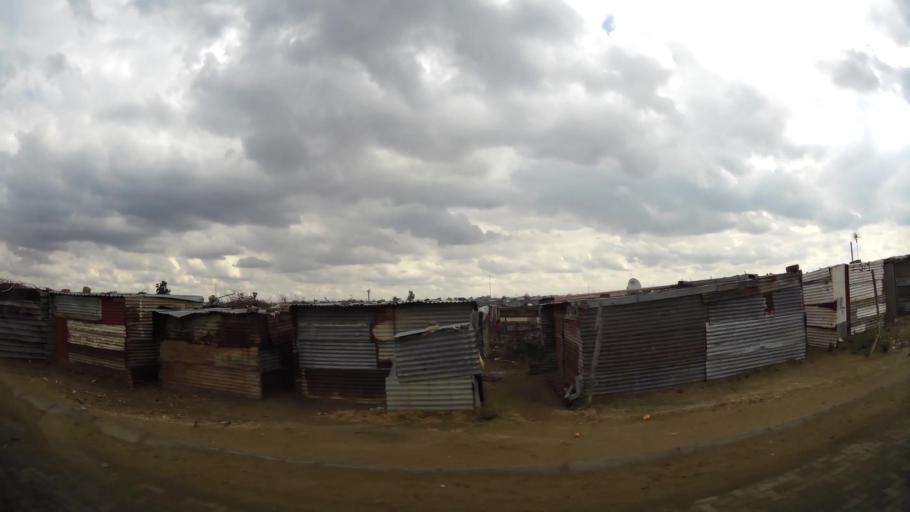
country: ZA
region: Orange Free State
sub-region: Fezile Dabi District Municipality
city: Sasolburg
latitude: -26.8613
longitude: 27.8729
